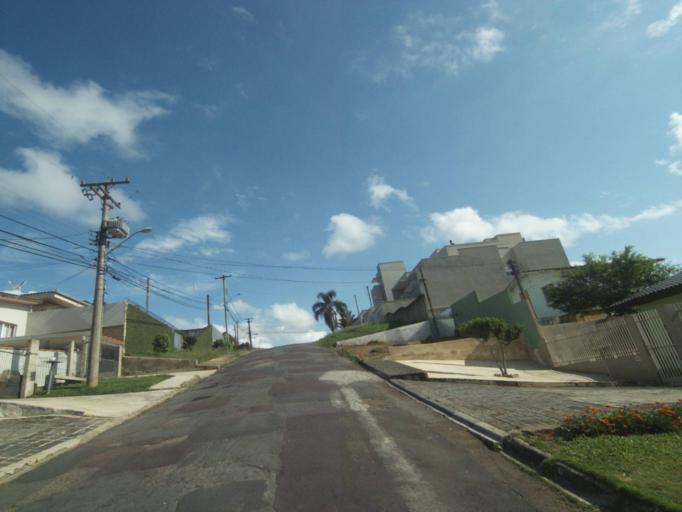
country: BR
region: Parana
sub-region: Curitiba
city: Curitiba
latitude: -25.3896
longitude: -49.3011
